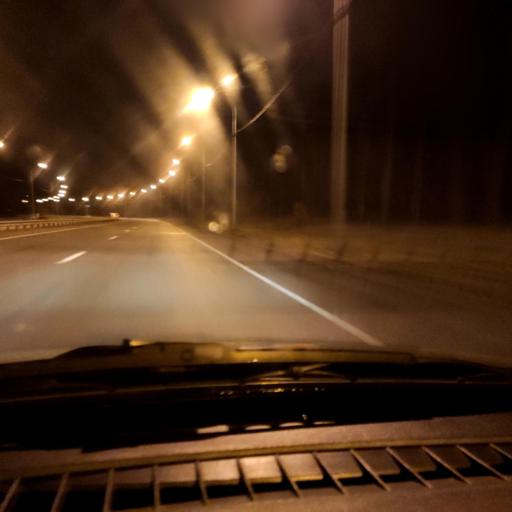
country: RU
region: Samara
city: Zhigulevsk
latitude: 53.5367
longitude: 49.5164
